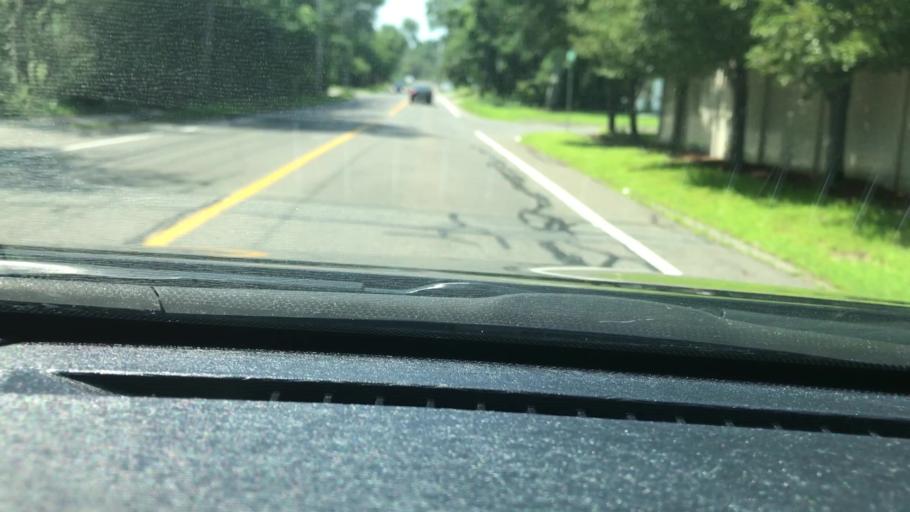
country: US
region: Massachusetts
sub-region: Middlesex County
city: Wakefield
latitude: 42.5109
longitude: -71.0590
